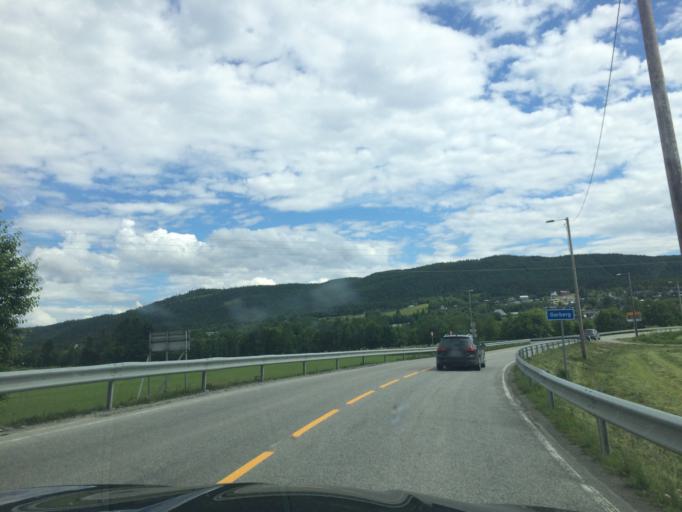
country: NO
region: Sor-Trondelag
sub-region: Selbu
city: Mebonden
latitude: 63.2541
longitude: 11.0884
